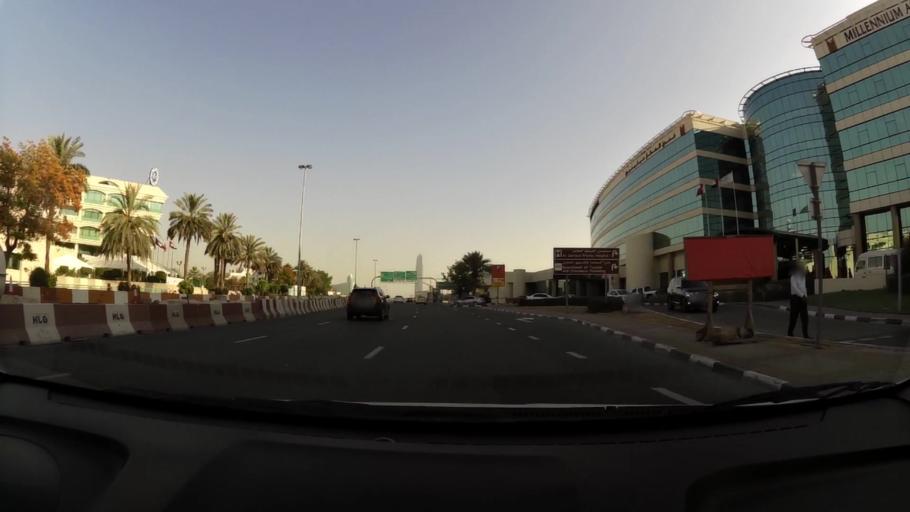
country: AE
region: Ash Shariqah
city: Sharjah
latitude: 25.2487
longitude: 55.3444
